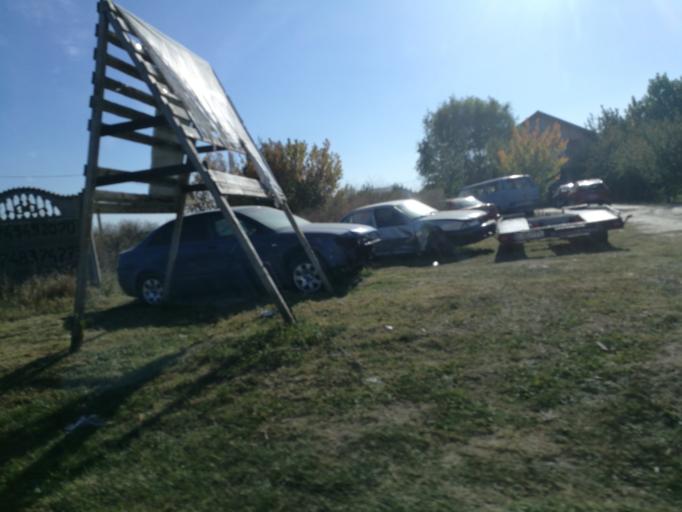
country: RO
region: Ilfov
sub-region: Comuna Dragomiresti-Vale
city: Dragomiresti-Vale
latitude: 44.4647
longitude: 25.9317
